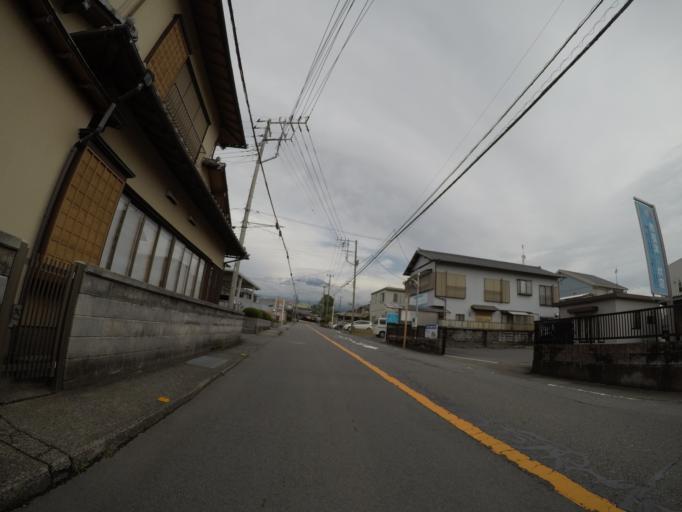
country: JP
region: Shizuoka
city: Fuji
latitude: 35.1929
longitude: 138.6521
